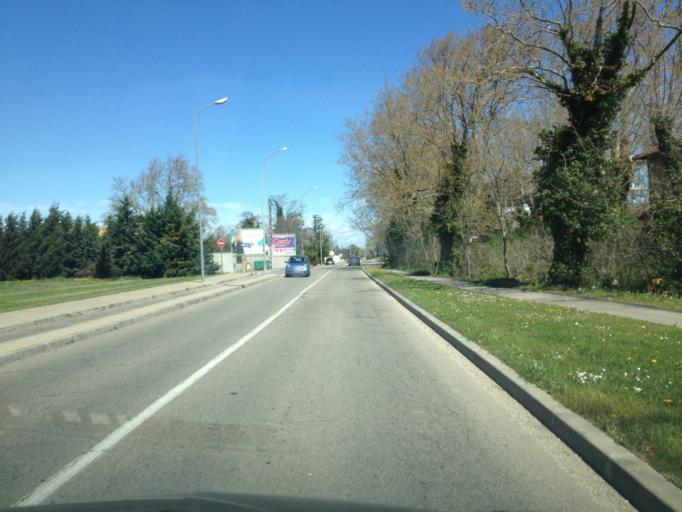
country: FR
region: Provence-Alpes-Cote d'Azur
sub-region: Departement du Vaucluse
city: Le Pontet
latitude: 43.9687
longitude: 4.8660
